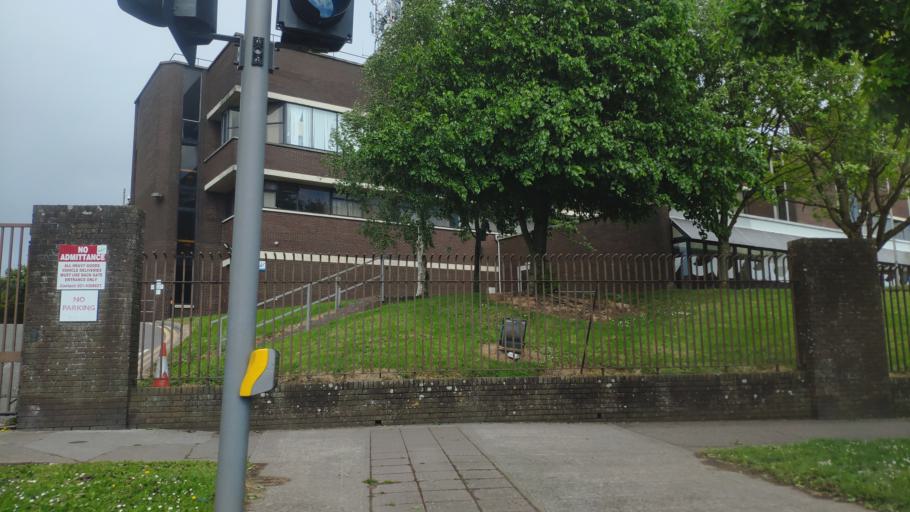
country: IE
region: Munster
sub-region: County Cork
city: Cork
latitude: 51.9124
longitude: -8.4890
